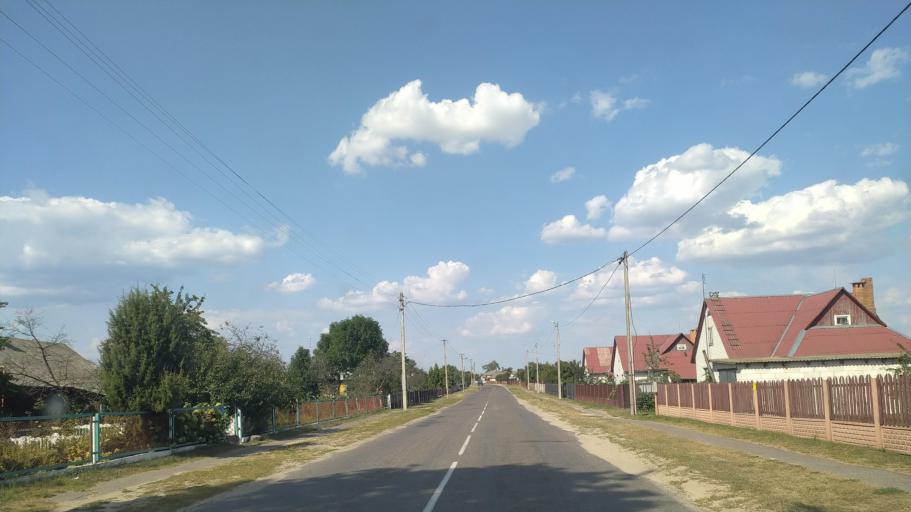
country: BY
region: Brest
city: Drahichyn
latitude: 52.1174
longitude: 25.1165
